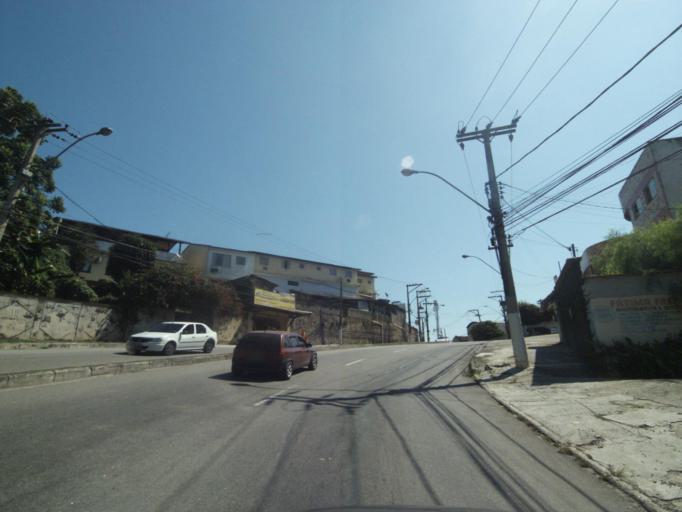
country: BR
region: Rio de Janeiro
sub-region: Niteroi
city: Niteroi
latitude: -22.9041
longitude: -43.0496
